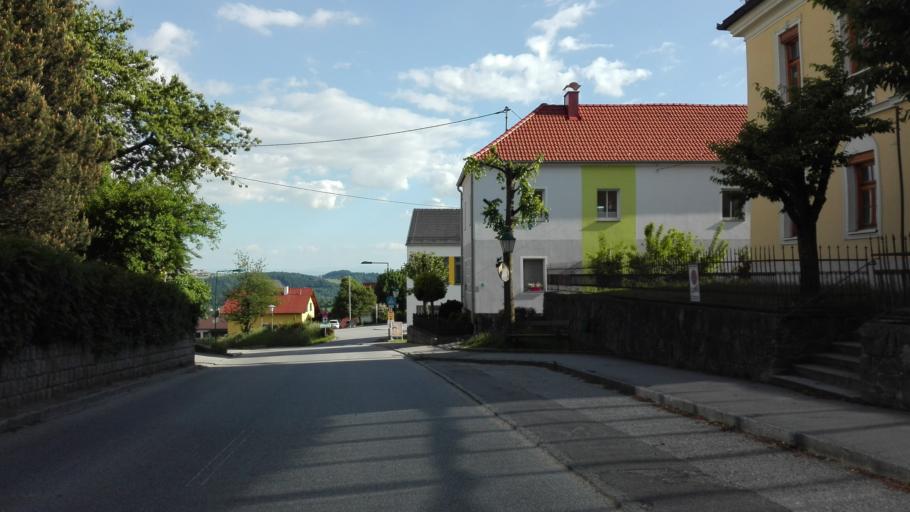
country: AT
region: Upper Austria
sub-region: Politischer Bezirk Perg
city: Perg
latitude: 48.3301
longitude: 14.6220
